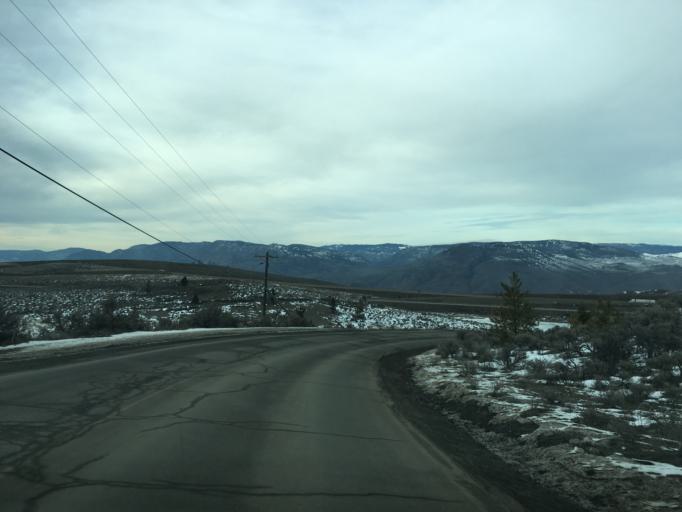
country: CA
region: British Columbia
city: Kamloops
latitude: 50.6604
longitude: -120.4357
